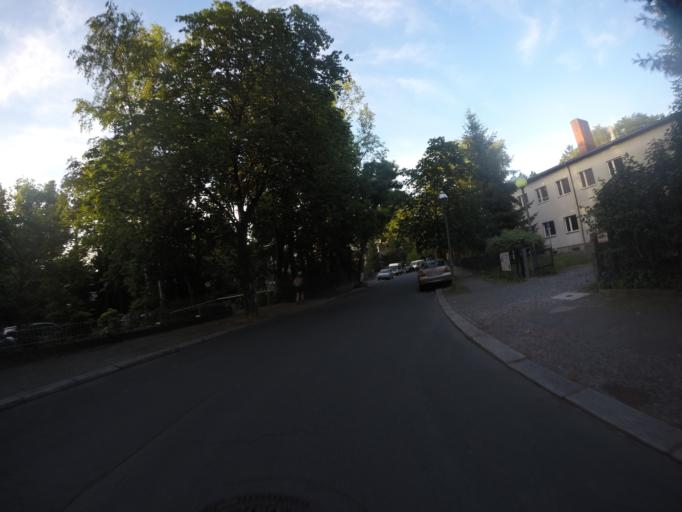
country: DE
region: Berlin
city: Grunewald
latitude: 52.4923
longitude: 13.2787
